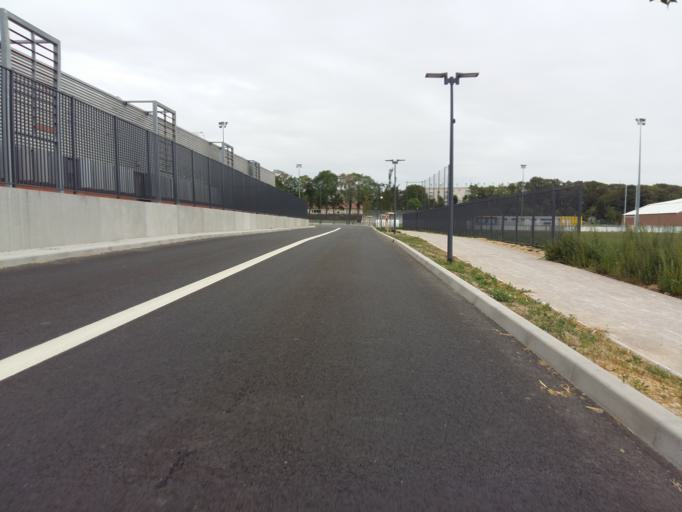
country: FR
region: Picardie
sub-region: Departement de la Somme
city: Amiens
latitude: 49.8741
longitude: 2.3015
